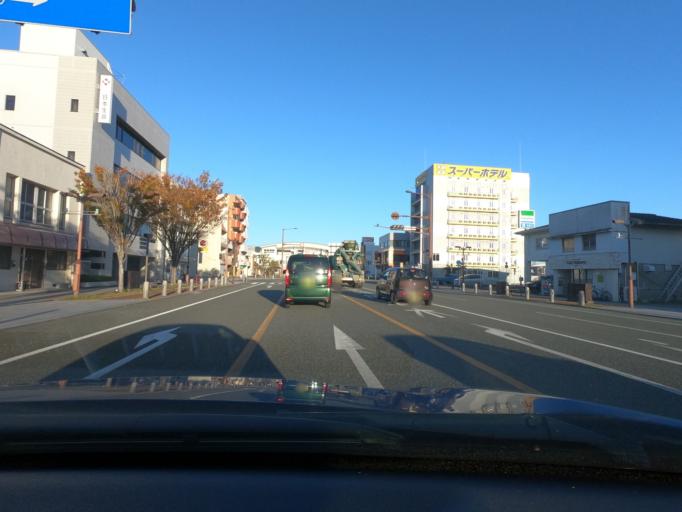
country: JP
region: Kagoshima
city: Satsumasendai
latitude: 31.8129
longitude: 130.3096
